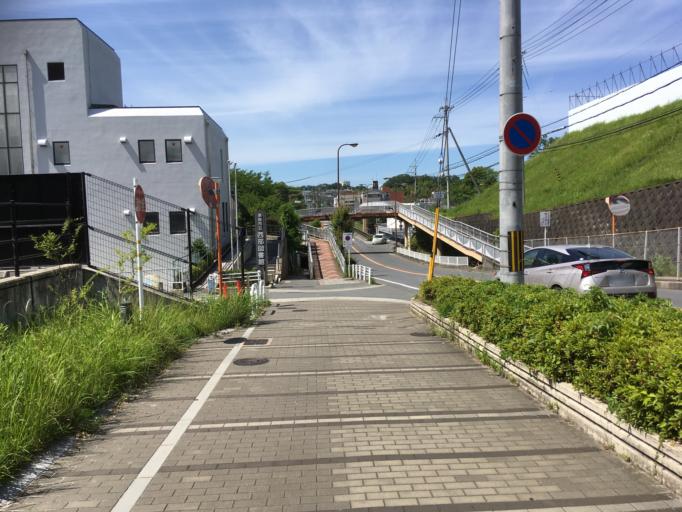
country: JP
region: Nara
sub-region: Ikoma-shi
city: Ikoma
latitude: 34.7053
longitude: 135.7503
